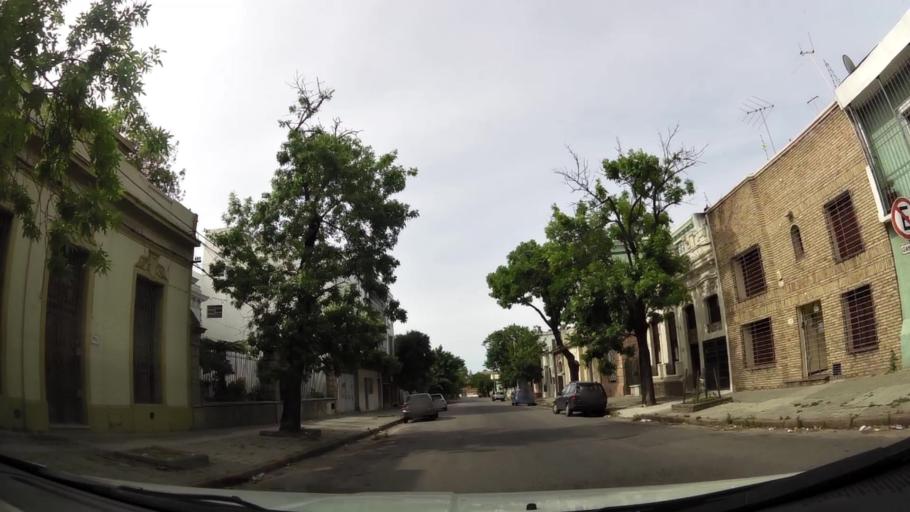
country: UY
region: Montevideo
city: Montevideo
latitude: -34.8770
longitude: -56.1996
